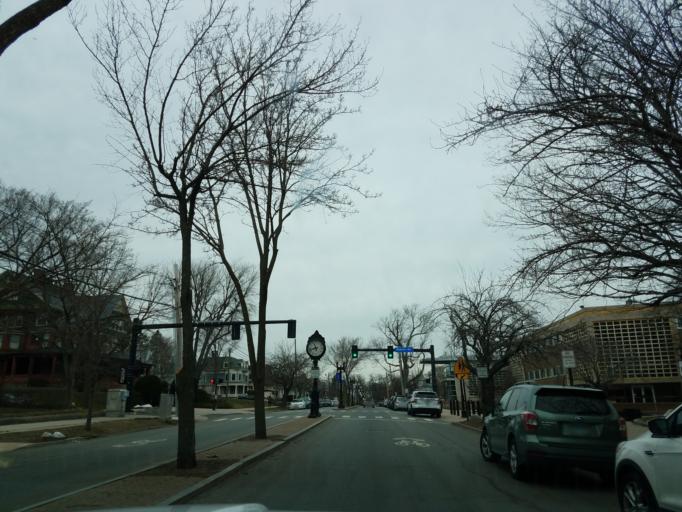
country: US
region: Connecticut
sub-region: Fairfield County
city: Bridgeport
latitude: 41.1652
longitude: -73.1911
